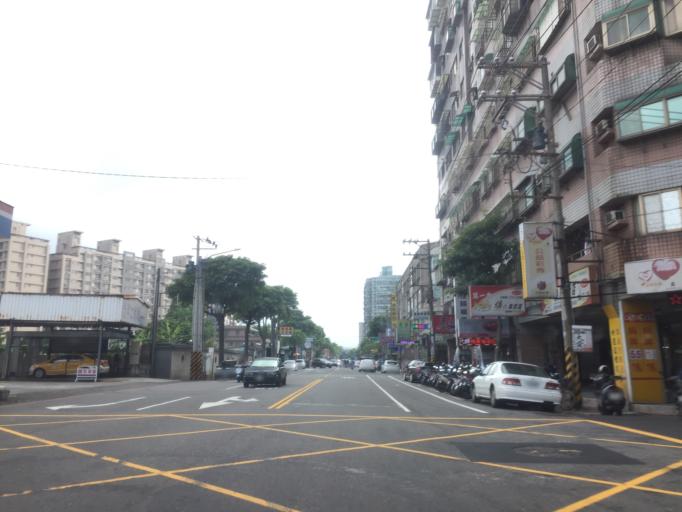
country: TW
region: Taiwan
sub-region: Taoyuan
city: Taoyuan
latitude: 24.9629
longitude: 121.3068
